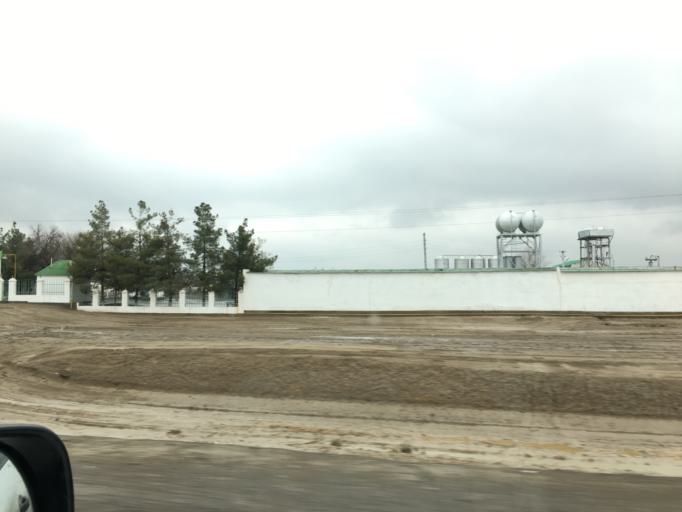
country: TM
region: Mary
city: Yoloeten
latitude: 37.3508
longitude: 62.2546
